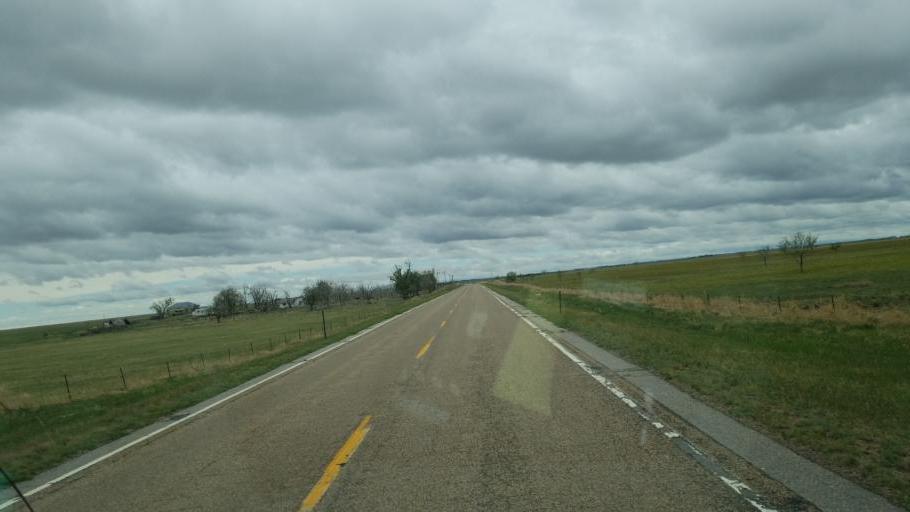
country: US
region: Colorado
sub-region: El Paso County
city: Ellicott
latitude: 38.8398
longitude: -103.9367
